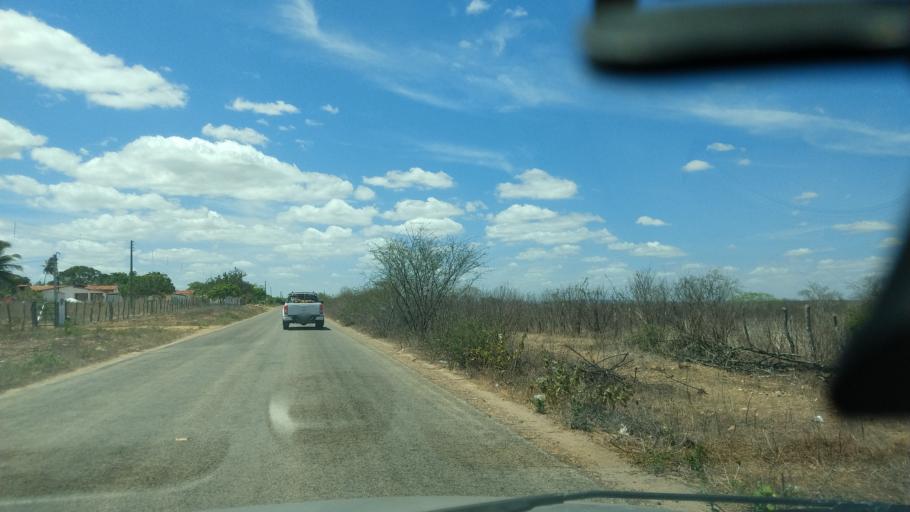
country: BR
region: Rio Grande do Norte
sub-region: Sao Paulo Do Potengi
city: Sao Paulo do Potengi
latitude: -5.9152
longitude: -35.7349
